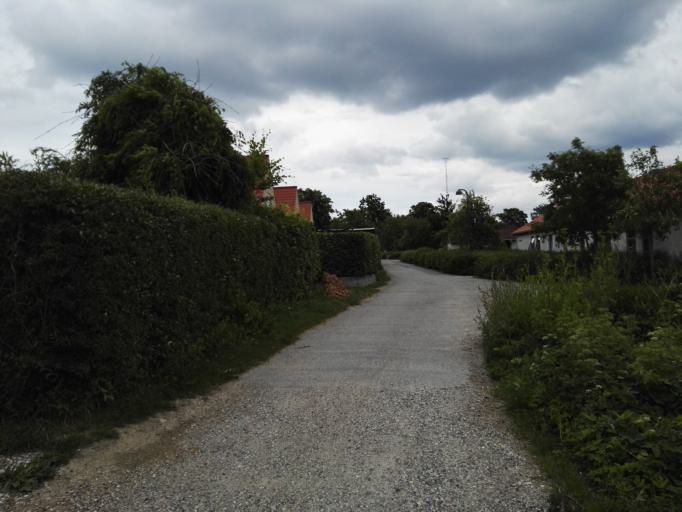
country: DK
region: Capital Region
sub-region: Egedal Kommune
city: Vekso
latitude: 55.7547
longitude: 12.2351
